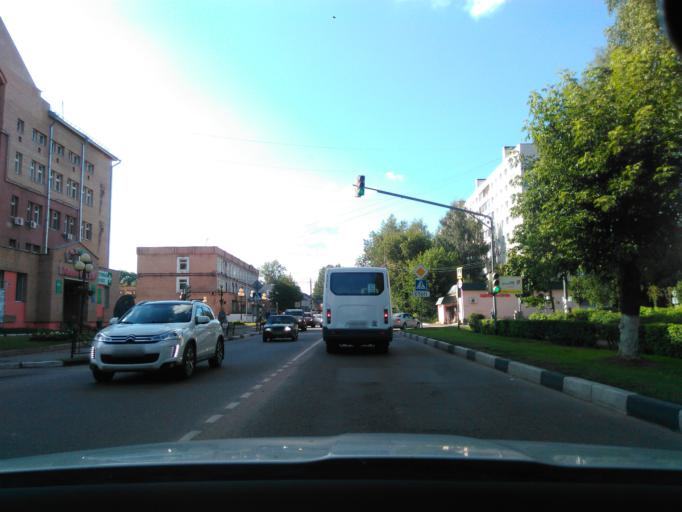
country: RU
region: Moskovskaya
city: Klin
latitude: 56.3232
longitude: 36.7204
